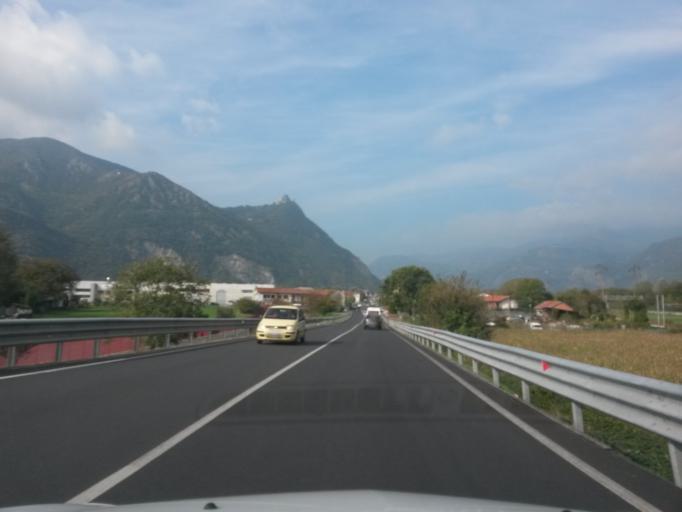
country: IT
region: Piedmont
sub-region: Provincia di Torino
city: Avigliana
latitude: 45.0910
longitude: 7.3841
